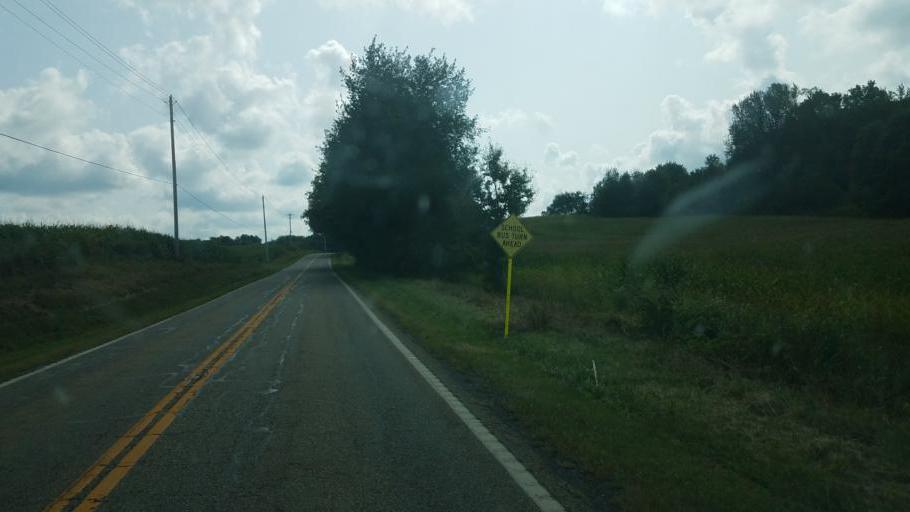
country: US
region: Ohio
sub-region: Stark County
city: Minerva
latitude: 40.7903
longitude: -81.0199
